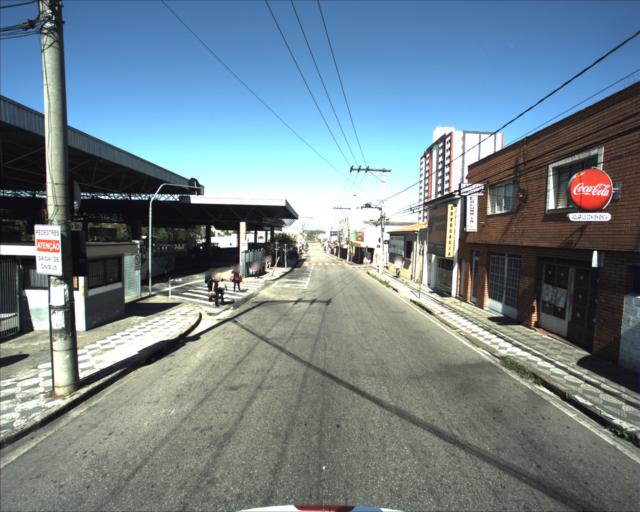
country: BR
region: Sao Paulo
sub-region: Sorocaba
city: Sorocaba
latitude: -23.5041
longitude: -47.4530
